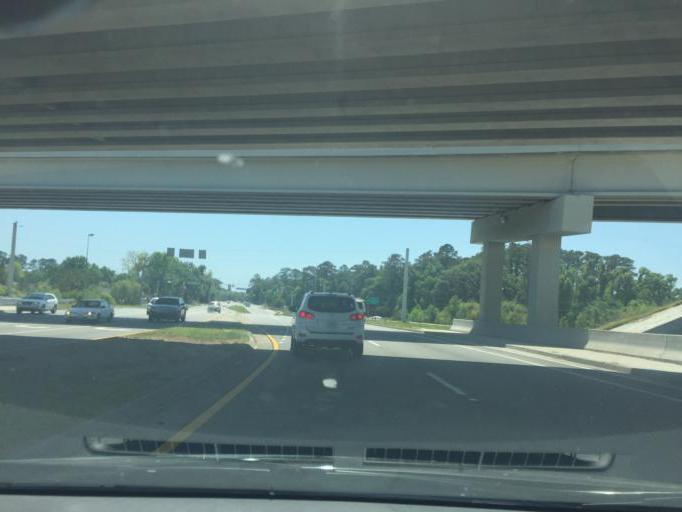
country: US
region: Georgia
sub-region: Chatham County
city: Montgomery
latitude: 31.9738
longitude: -81.1059
